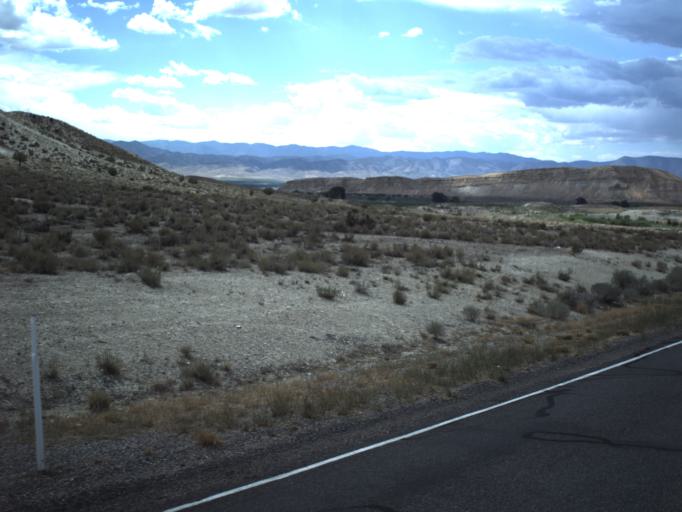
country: US
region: Utah
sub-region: Sanpete County
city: Gunnison
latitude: 39.1465
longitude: -111.7375
